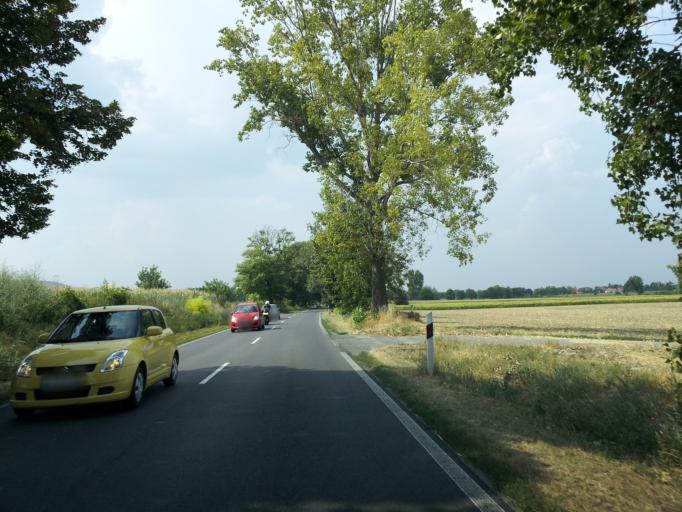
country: HU
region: Gyor-Moson-Sopron
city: Nyul
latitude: 47.5705
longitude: 17.7012
